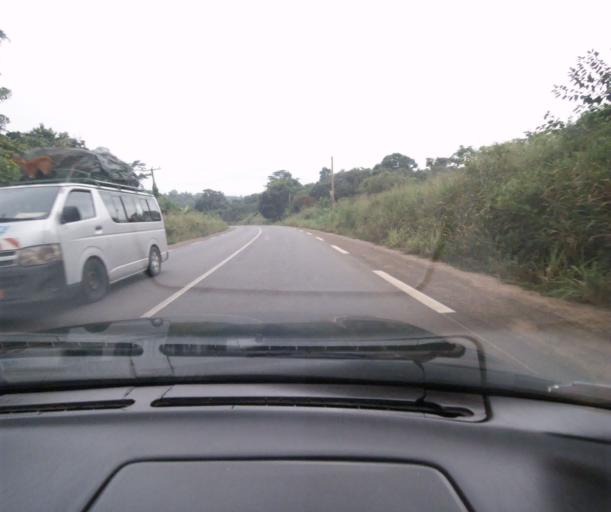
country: CM
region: Centre
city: Obala
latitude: 4.1946
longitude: 11.4527
